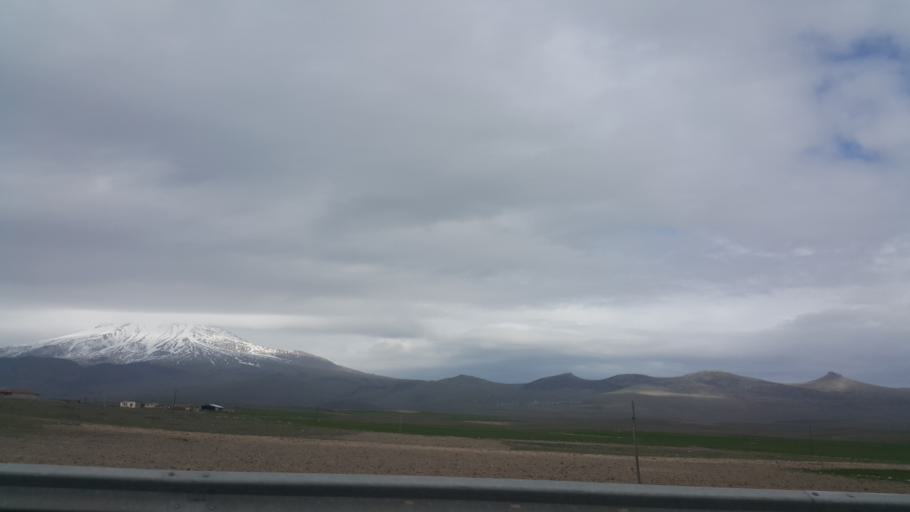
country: TR
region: Aksaray
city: Taspinar
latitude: 38.0898
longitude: 34.0331
